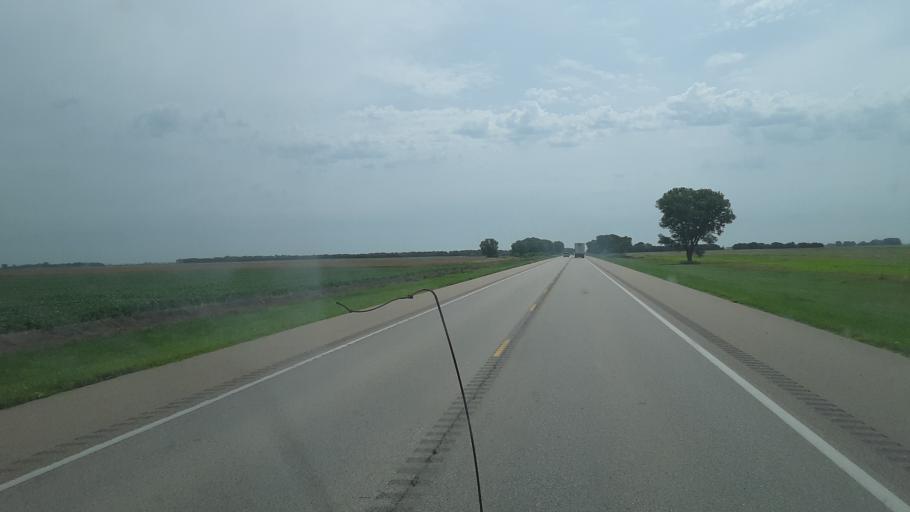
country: US
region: Kansas
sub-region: Reno County
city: Nickerson
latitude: 37.9850
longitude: -98.1948
